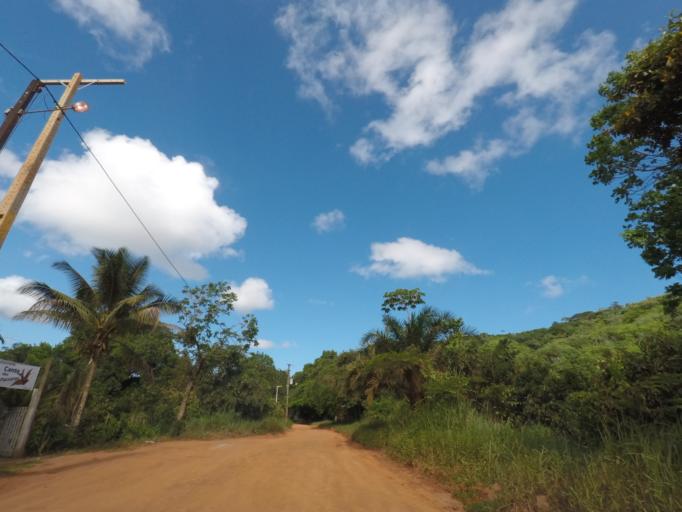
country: BR
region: Bahia
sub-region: Itacare
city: Itacare
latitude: -14.2111
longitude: -39.0520
